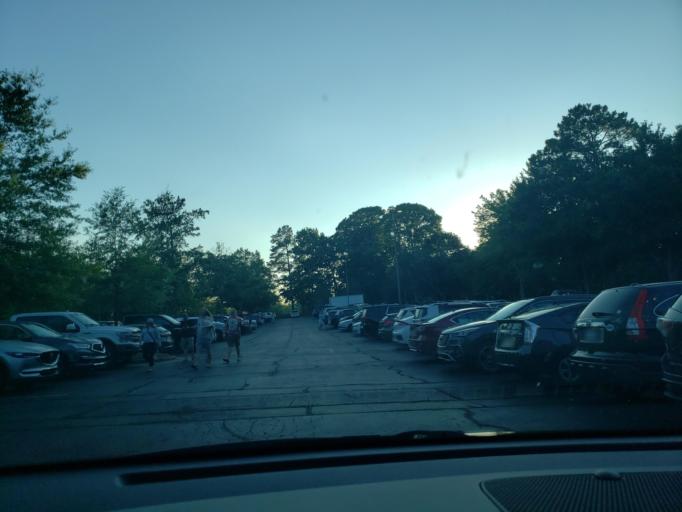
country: US
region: North Carolina
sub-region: Wake County
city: Apex
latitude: 35.7299
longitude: -78.7974
